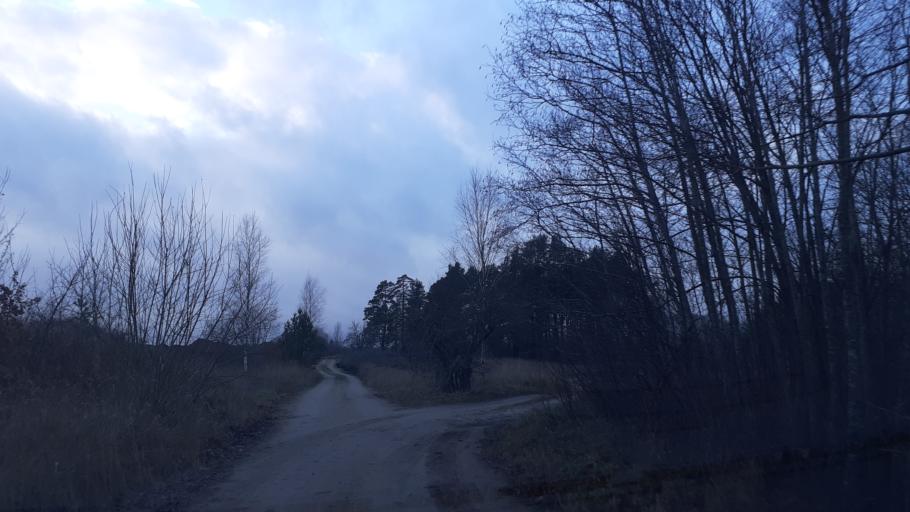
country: LV
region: Talsu Rajons
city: Stende
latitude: 57.0655
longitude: 22.2714
